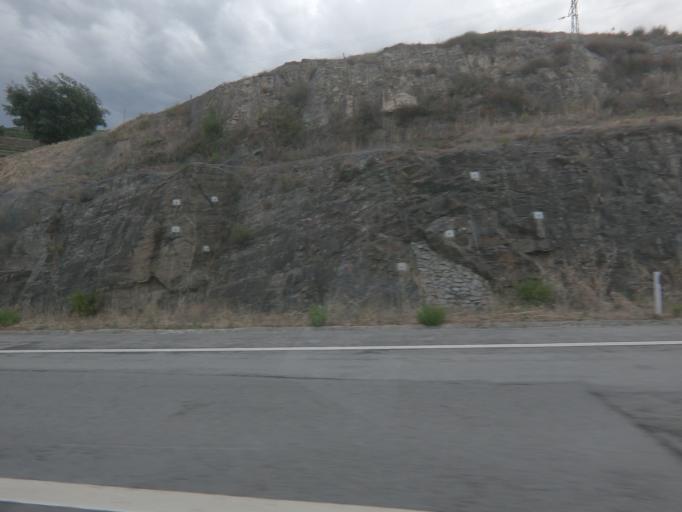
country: PT
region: Vila Real
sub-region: Peso da Regua
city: Peso da Regua
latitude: 41.1336
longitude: -7.7721
